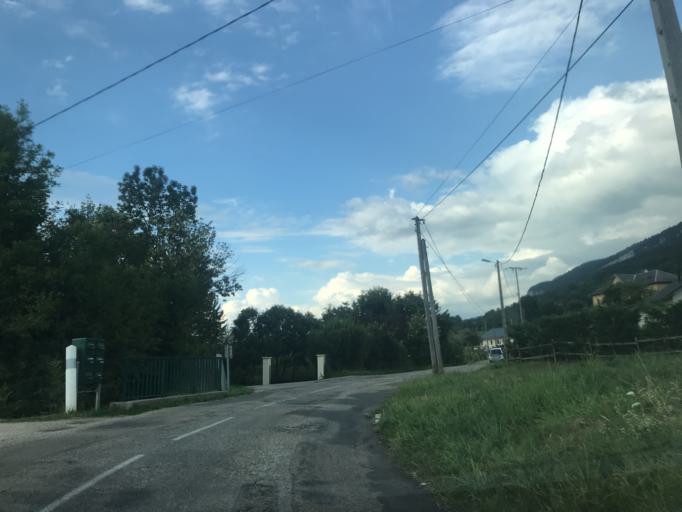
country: FR
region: Rhone-Alpes
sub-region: Departement de la Haute-Savoie
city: Cusy
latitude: 45.7246
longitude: 6.0044
